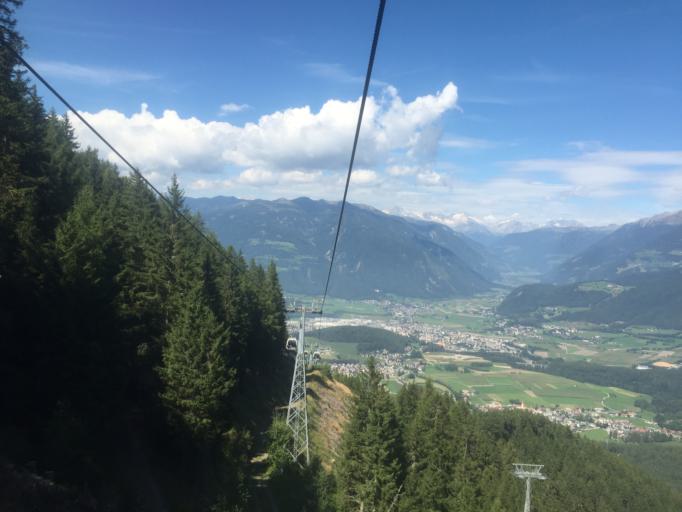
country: IT
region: Trentino-Alto Adige
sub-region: Bolzano
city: Riscone
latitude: 46.7543
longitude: 11.9495
